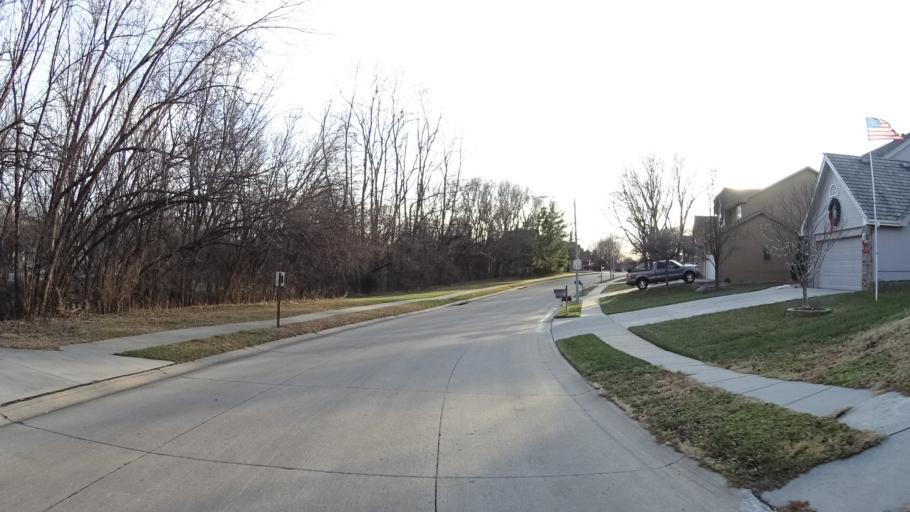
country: US
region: Nebraska
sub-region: Sarpy County
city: La Vista
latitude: 41.1829
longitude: -95.9834
